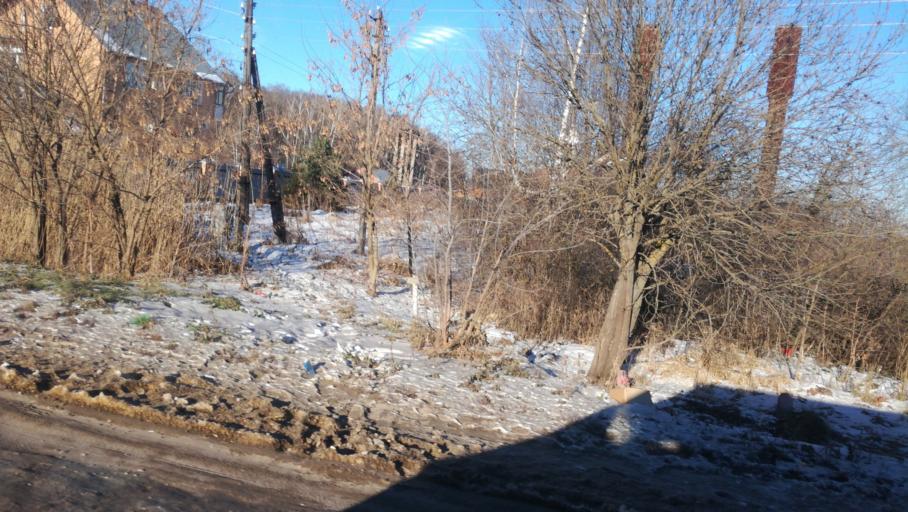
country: RU
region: Tula
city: Kosaya Gora
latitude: 54.1701
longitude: 37.4784
